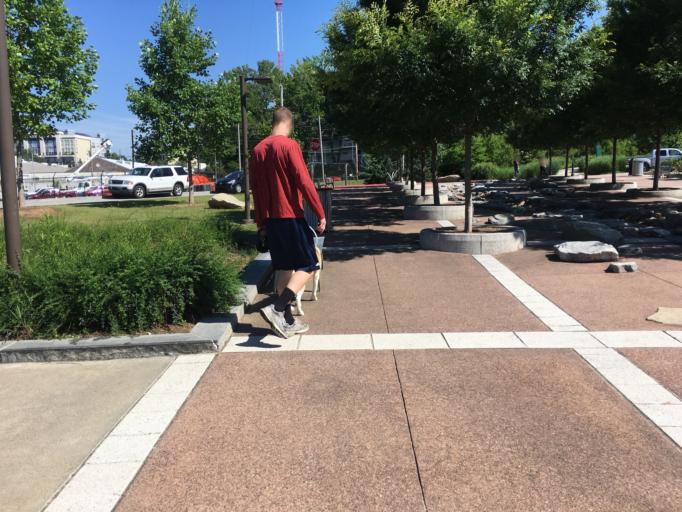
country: US
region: Georgia
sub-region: Fulton County
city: Atlanta
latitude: 33.7678
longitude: -84.3649
